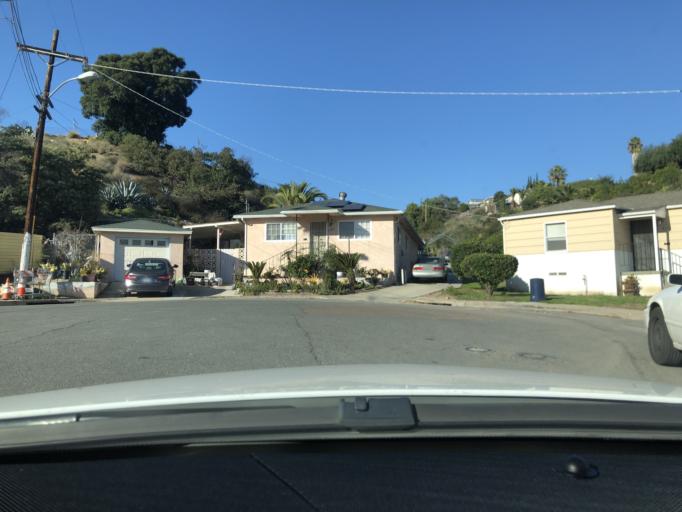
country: US
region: California
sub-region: San Diego County
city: Lemon Grove
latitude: 32.7535
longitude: -117.0672
